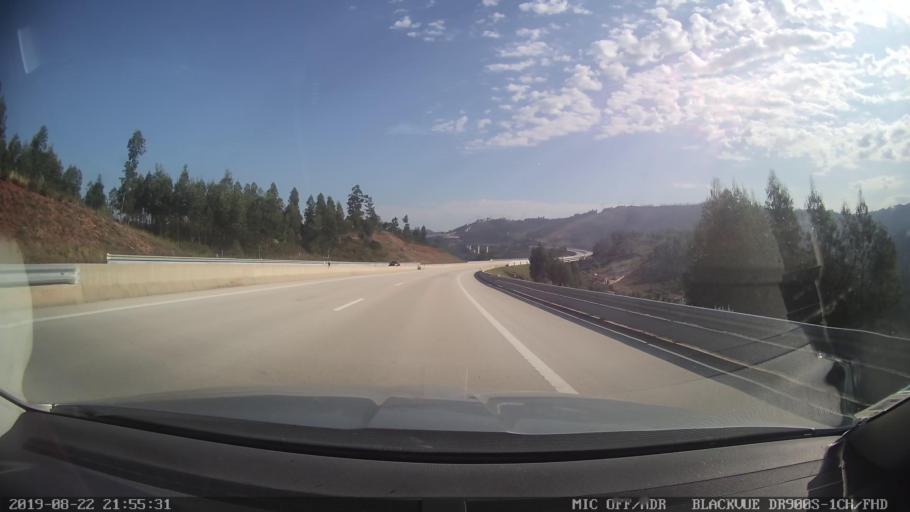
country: PT
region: Coimbra
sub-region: Coimbra
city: Coimbra
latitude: 40.1547
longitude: -8.3847
